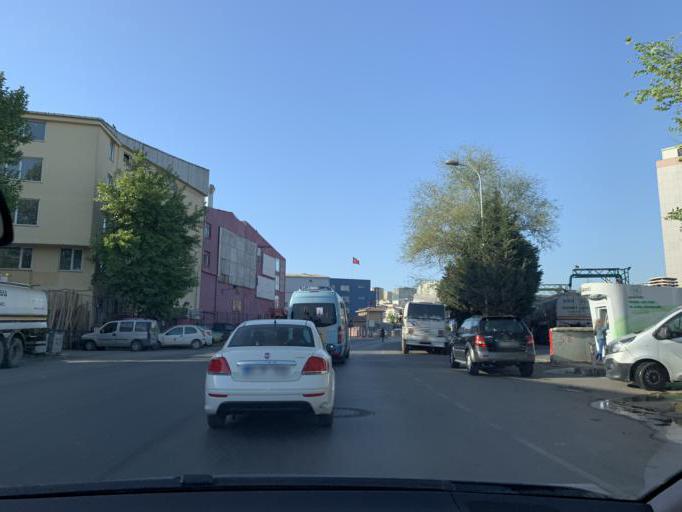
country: TR
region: Istanbul
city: Icmeler
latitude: 40.8473
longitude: 29.2936
